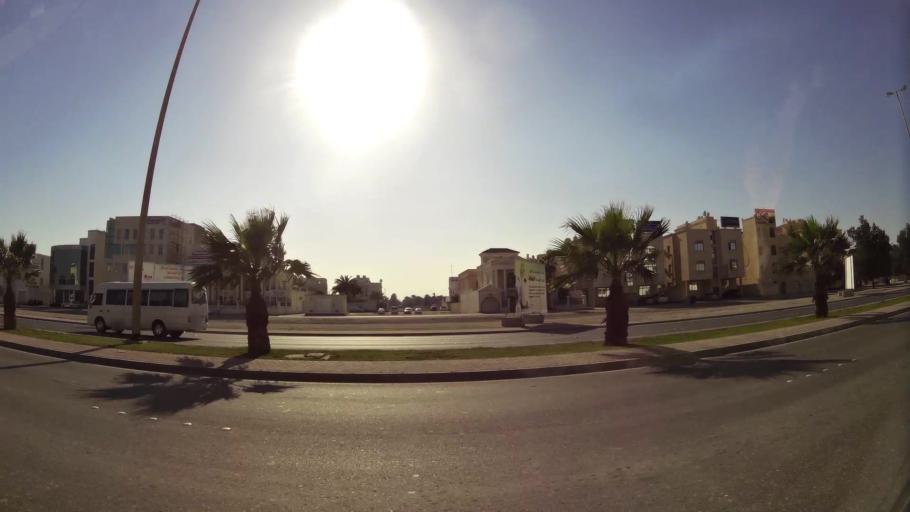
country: BH
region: Manama
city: Manama
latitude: 26.2091
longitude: 50.5669
